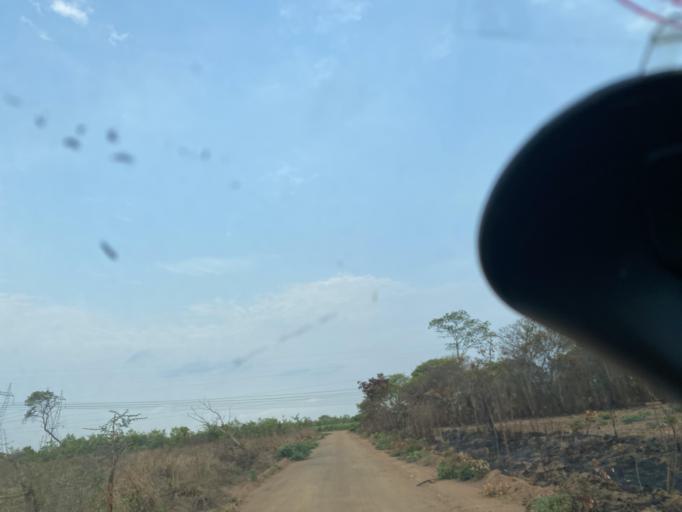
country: ZM
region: Lusaka
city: Chongwe
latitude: -15.2043
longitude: 28.5177
